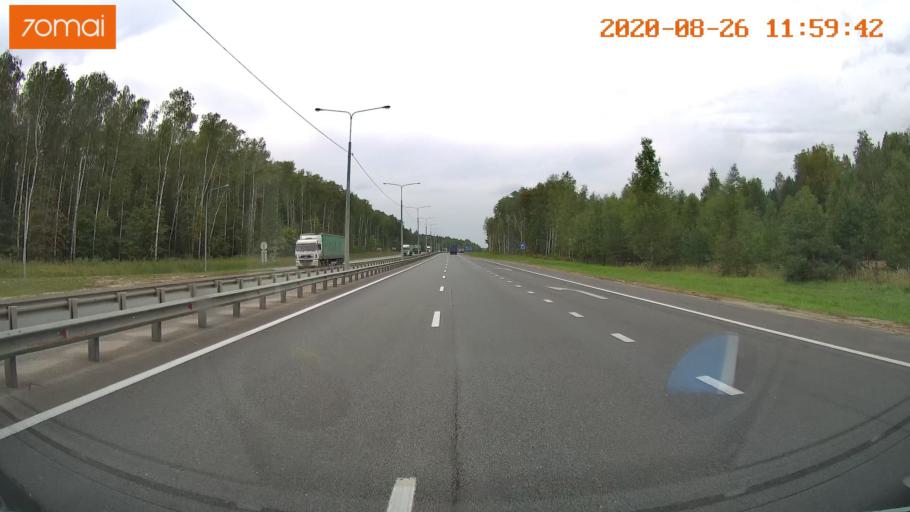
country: RU
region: Rjazan
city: Kiritsy
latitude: 54.2861
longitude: 40.2928
